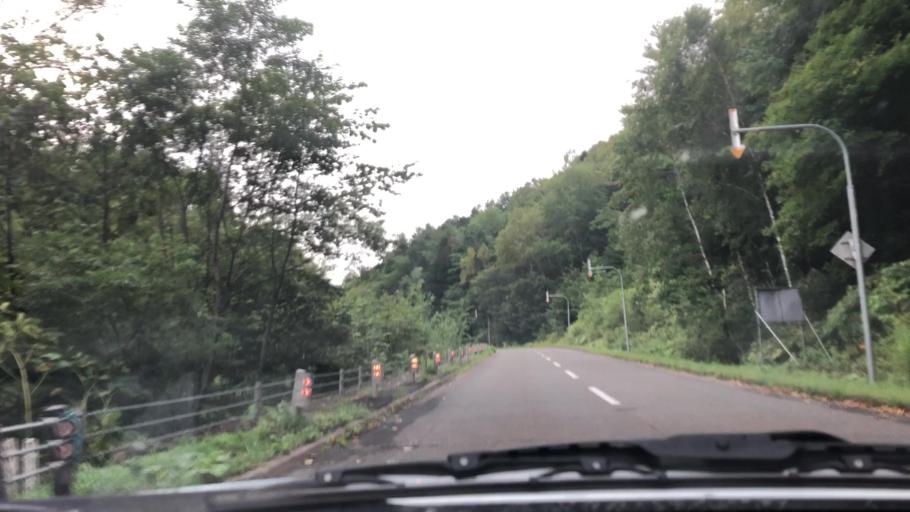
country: JP
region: Hokkaido
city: Shimo-furano
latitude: 42.9426
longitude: 142.3739
